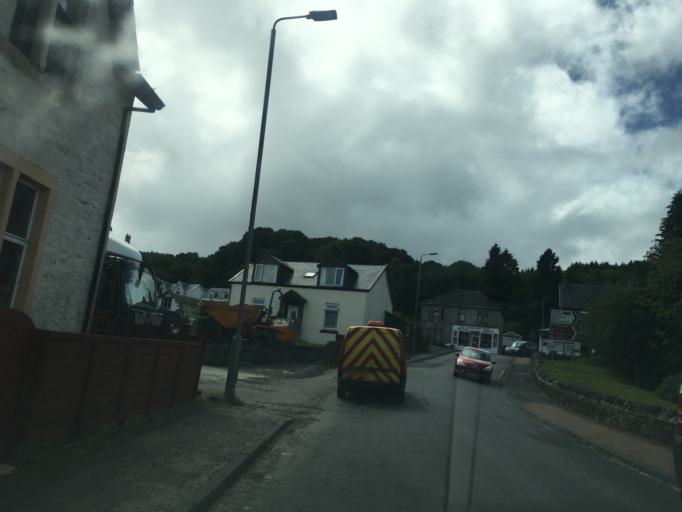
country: GB
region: Scotland
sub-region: Argyll and Bute
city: Dunoon
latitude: 55.9815
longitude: -4.9472
